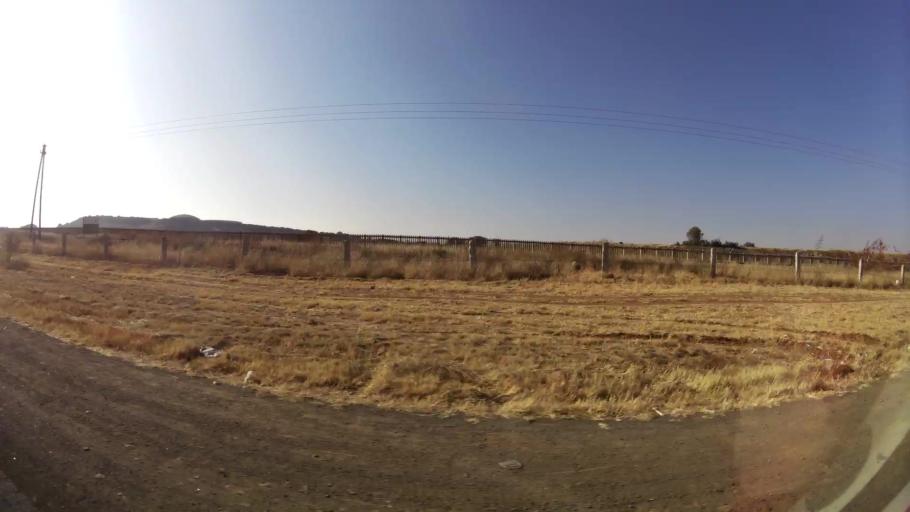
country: ZA
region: Orange Free State
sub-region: Mangaung Metropolitan Municipality
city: Bloemfontein
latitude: -29.1782
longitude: 26.1911
